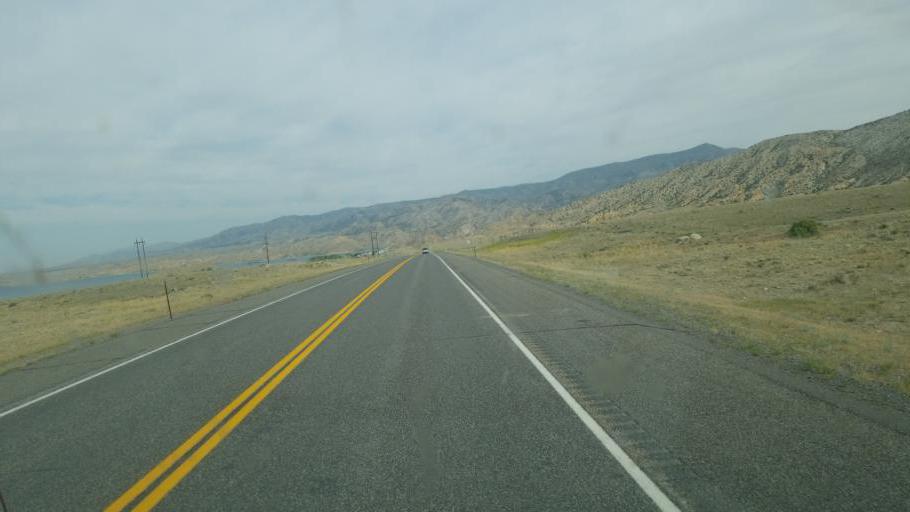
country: US
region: Wyoming
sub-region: Hot Springs County
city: Thermopolis
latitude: 43.3828
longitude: -108.1415
